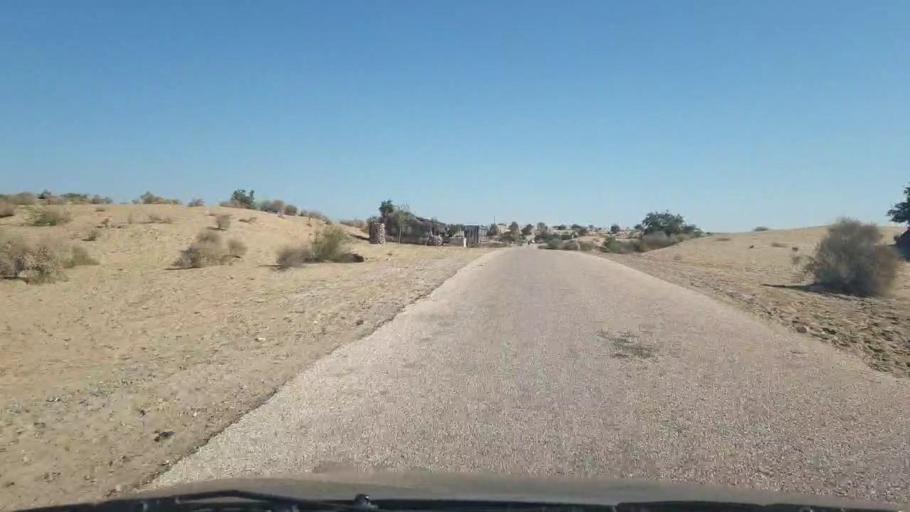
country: PK
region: Sindh
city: Bozdar
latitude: 27.0062
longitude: 68.9050
